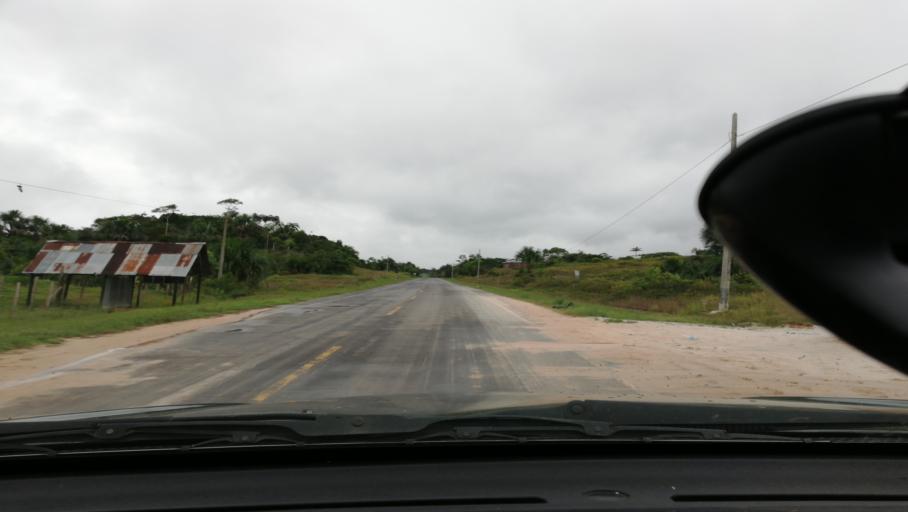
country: PE
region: Loreto
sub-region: Provincia de Loreto
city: Nauta
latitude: -4.3436
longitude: -73.5400
